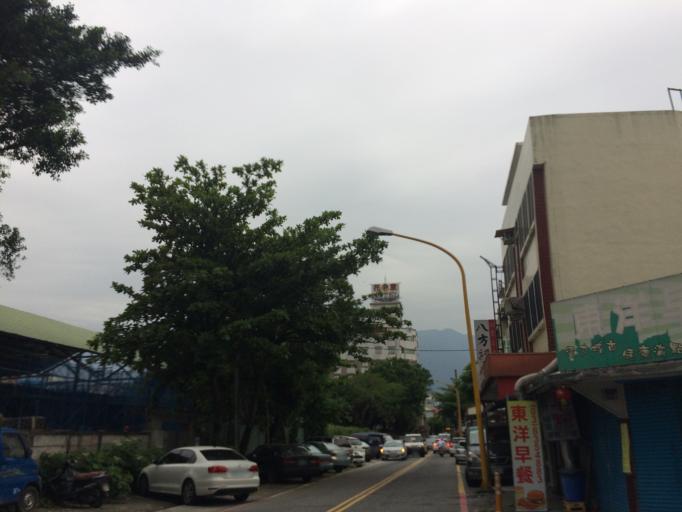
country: TW
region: Taiwan
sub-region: Hualien
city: Hualian
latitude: 23.9798
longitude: 121.6093
